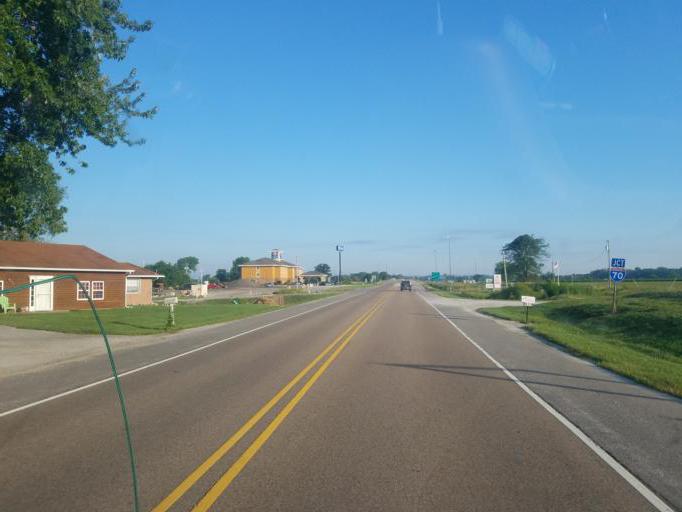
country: US
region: Illinois
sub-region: Bond County
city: Greenville
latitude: 38.8671
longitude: -89.3807
